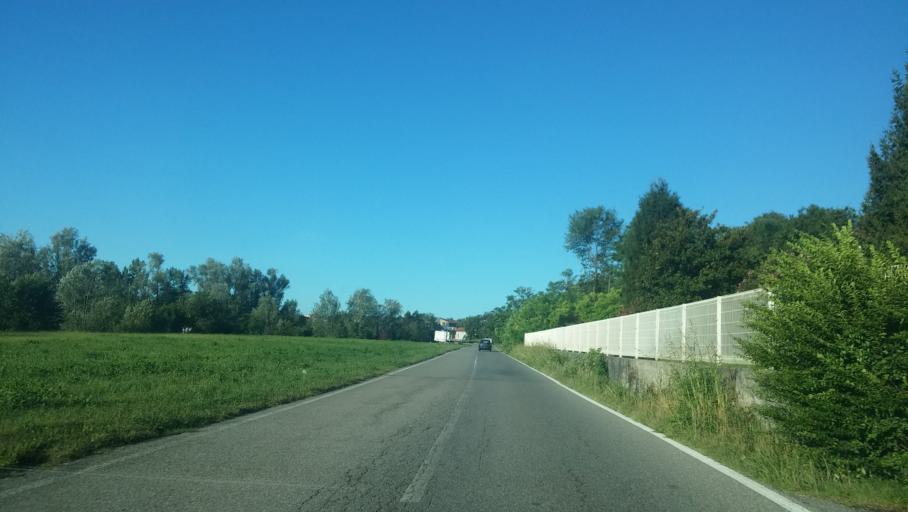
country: IT
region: Lombardy
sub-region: Provincia di Lecco
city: Suello
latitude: 45.8235
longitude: 9.3245
